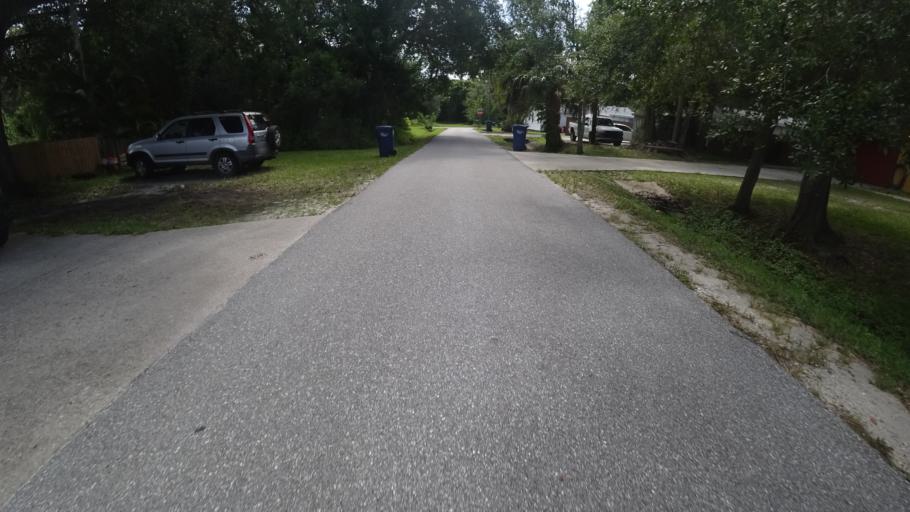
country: US
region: Florida
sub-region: Manatee County
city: Samoset
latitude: 27.4531
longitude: -82.5395
